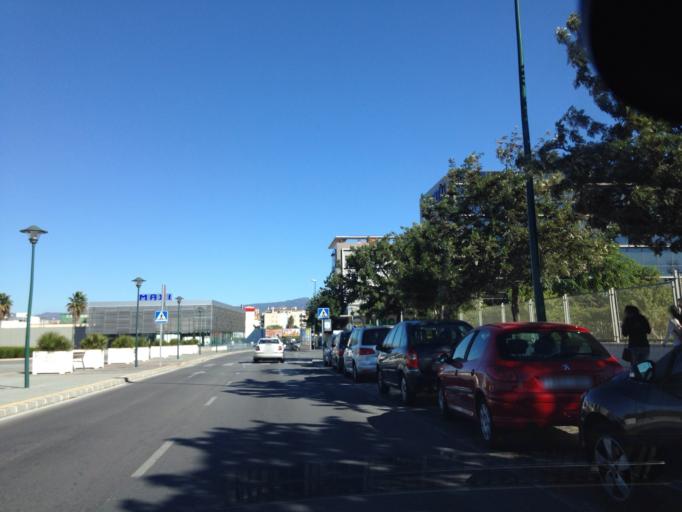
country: ES
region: Andalusia
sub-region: Provincia de Malaga
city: Malaga
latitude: 36.6837
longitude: -4.4586
